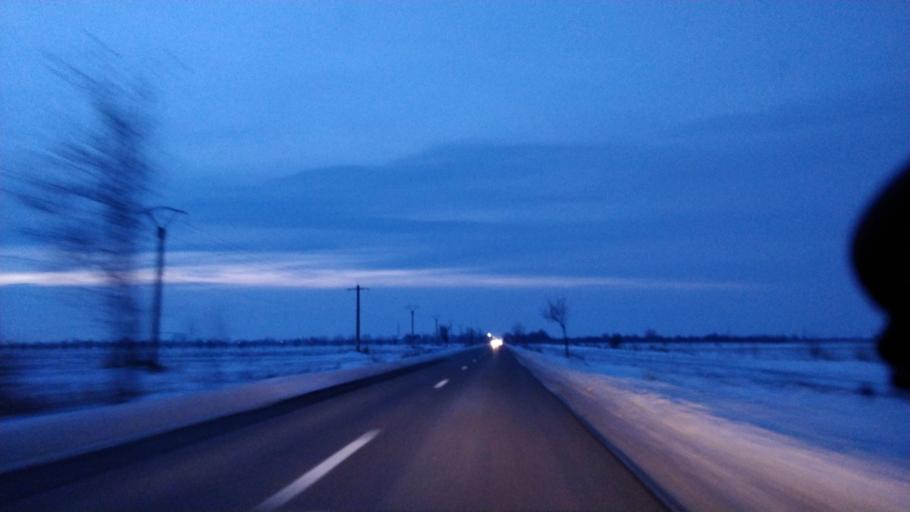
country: RO
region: Vrancea
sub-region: Comuna Vulturu
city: Vadu Rosca
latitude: 45.6048
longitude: 27.4513
